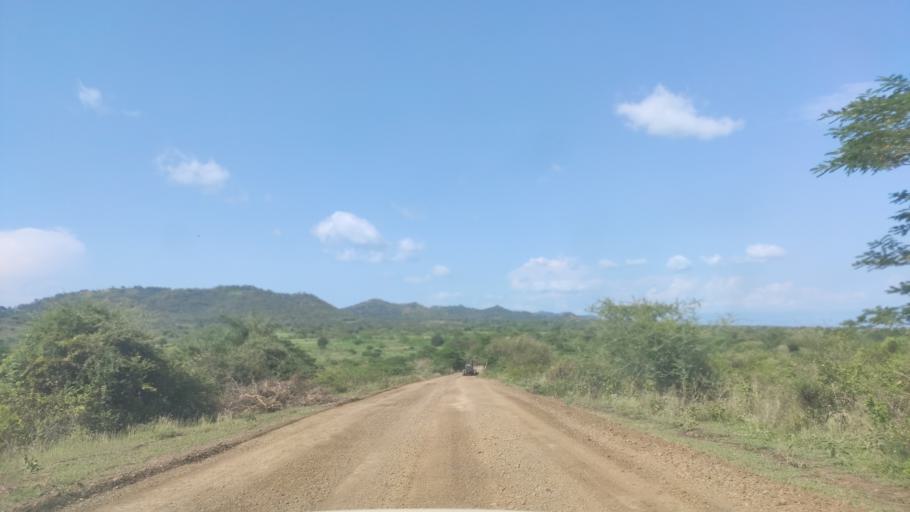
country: ET
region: Southern Nations, Nationalities, and People's Region
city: Felege Neway
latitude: 6.3865
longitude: 37.0960
